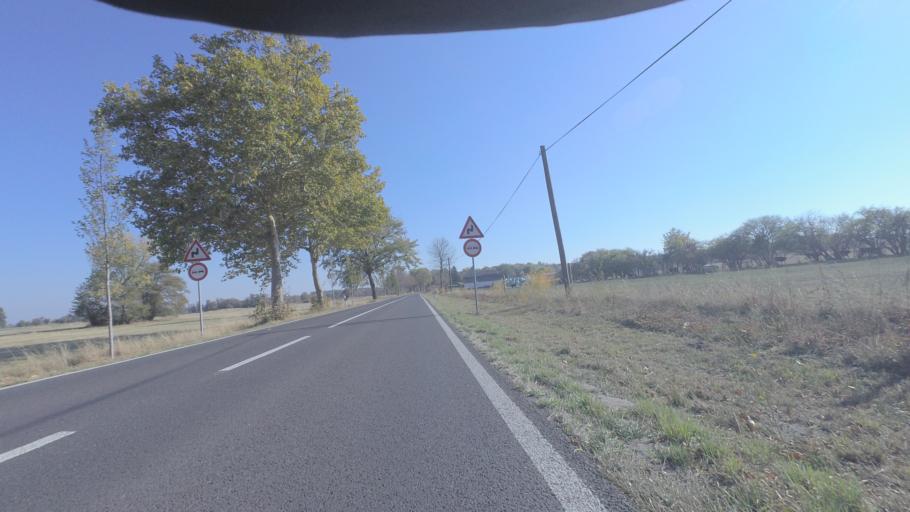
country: DE
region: Brandenburg
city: Zossen
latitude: 52.2569
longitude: 13.4574
